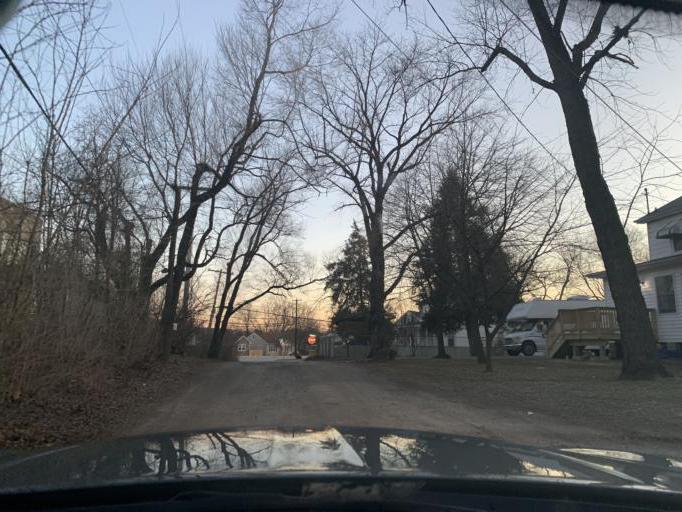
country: US
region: Maryland
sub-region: Anne Arundel County
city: Glen Burnie
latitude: 39.1506
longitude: -76.6374
